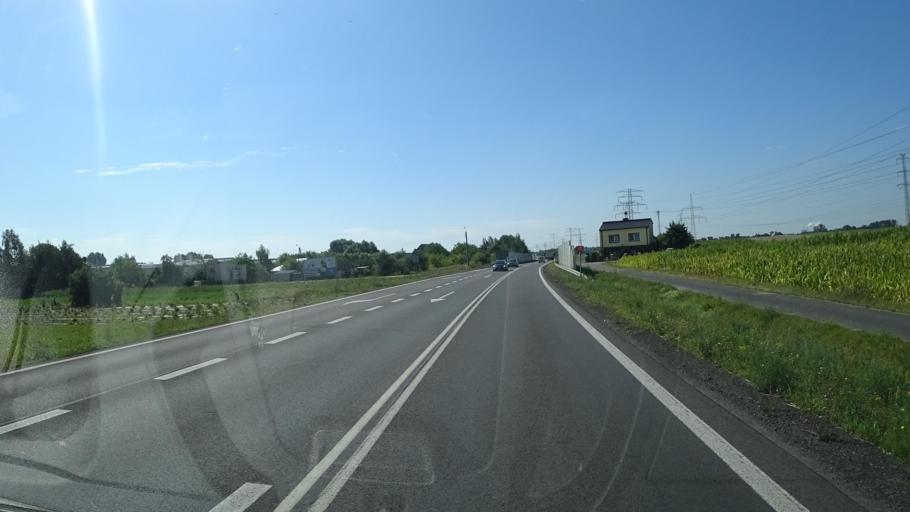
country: PL
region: Greater Poland Voivodeship
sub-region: Powiat koninski
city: Slesin
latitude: 52.3698
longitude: 18.2964
